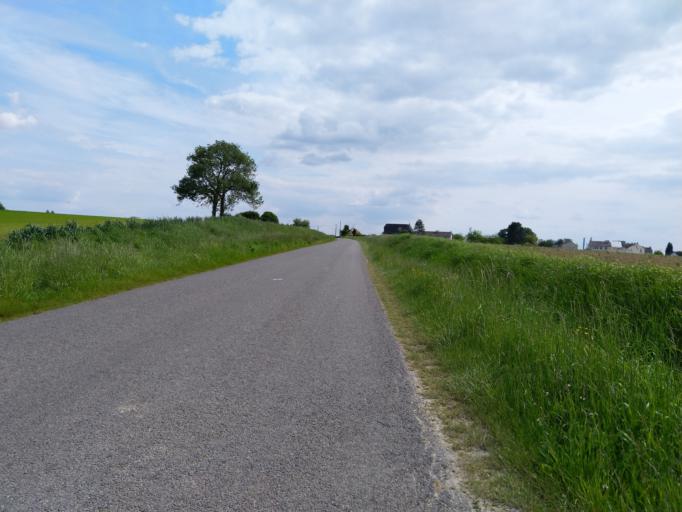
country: FR
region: Picardie
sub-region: Departement de l'Aisne
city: Boue
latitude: 50.0177
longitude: 3.6926
